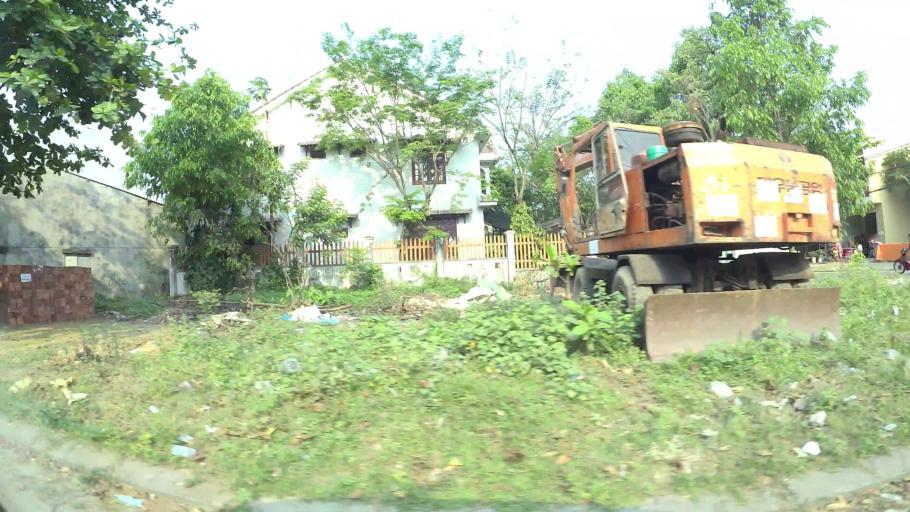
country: VN
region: Da Nang
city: Lien Chieu
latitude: 16.0539
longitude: 108.1669
